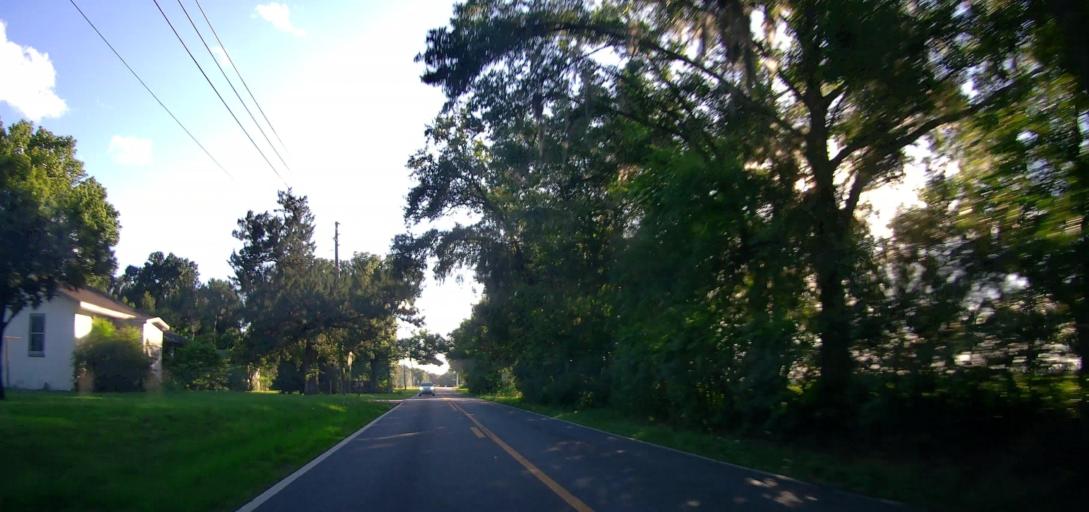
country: US
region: Florida
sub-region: Marion County
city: Silver Springs Shores
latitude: 29.0647
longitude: -82.0137
